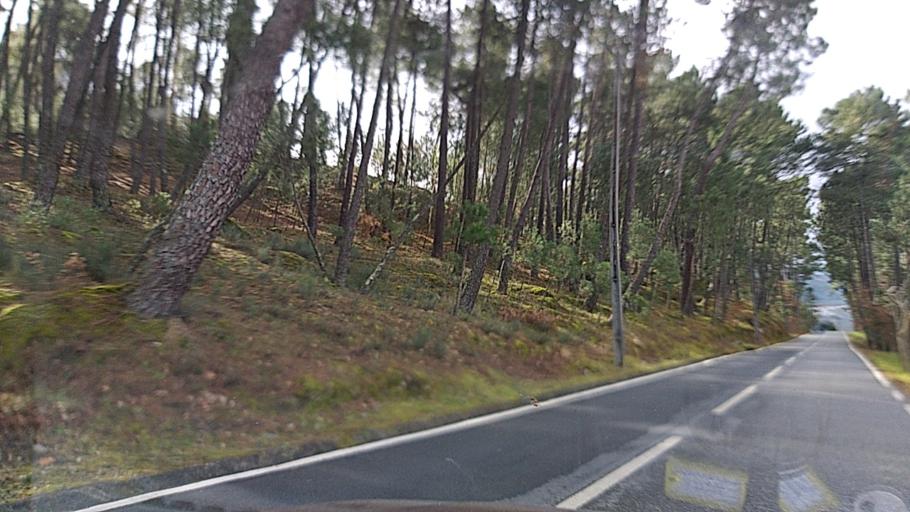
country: PT
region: Viseu
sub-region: Satao
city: Satao
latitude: 40.6602
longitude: -7.6522
